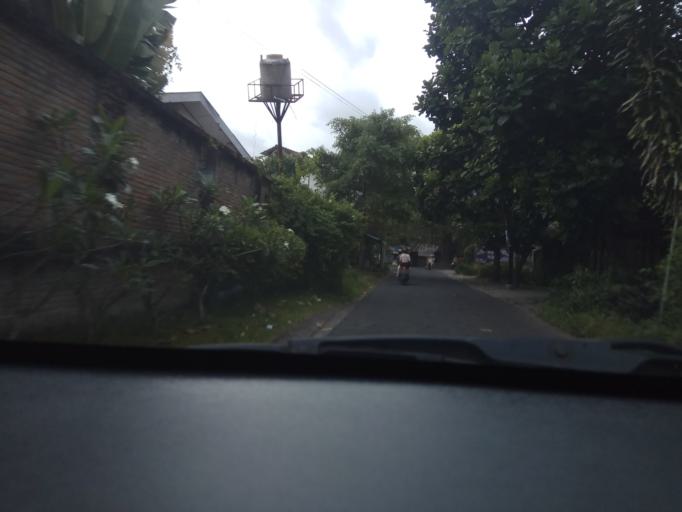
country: ID
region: Daerah Istimewa Yogyakarta
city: Depok
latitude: -7.7624
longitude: 110.3943
